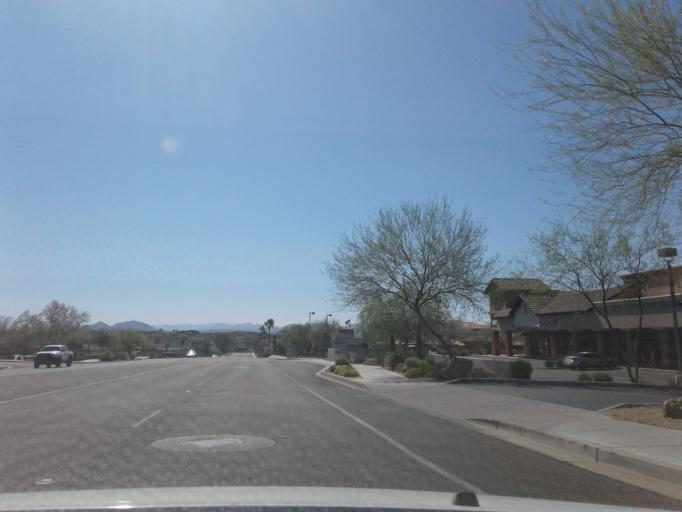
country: US
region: Arizona
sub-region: Maricopa County
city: Fountain Hills
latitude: 33.6091
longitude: -111.7220
